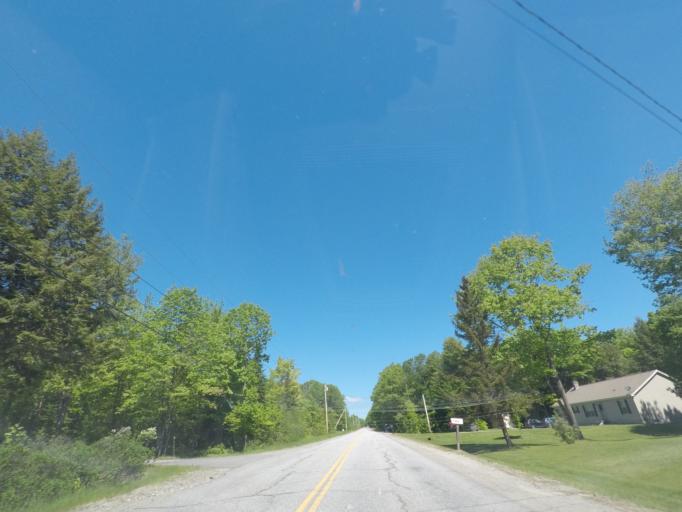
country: US
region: Maine
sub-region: Kennebec County
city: Manchester
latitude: 44.2313
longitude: -69.8813
